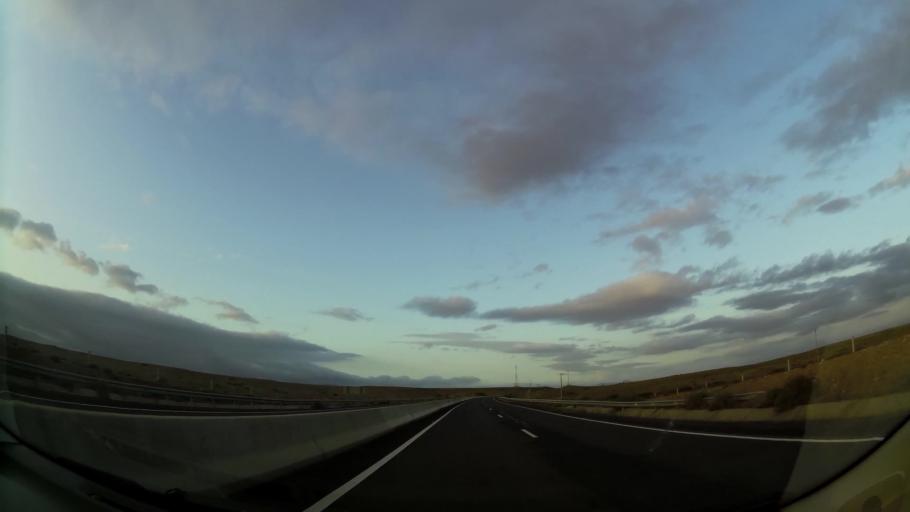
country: MA
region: Oriental
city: Taourirt
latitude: 34.5427
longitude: -2.9085
